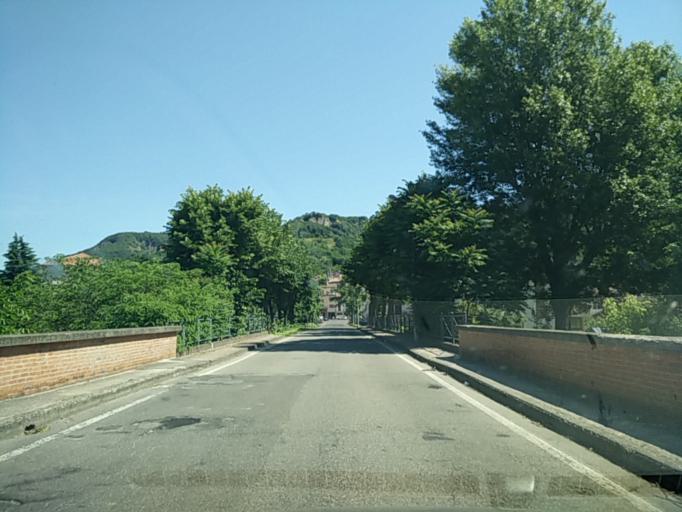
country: IT
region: Lombardy
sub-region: Provincia di Pavia
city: Godiasco
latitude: 44.8942
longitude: 9.0548
